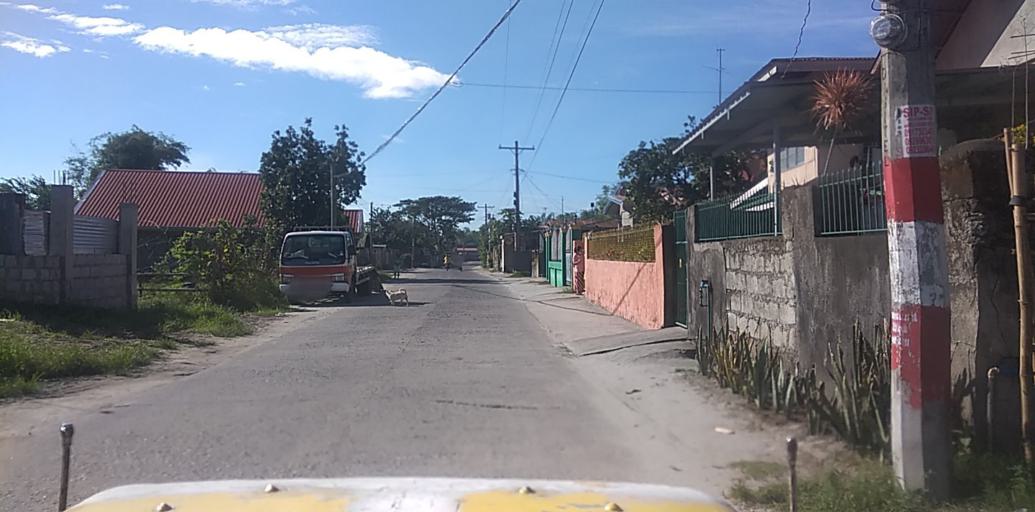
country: PH
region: Central Luzon
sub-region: Province of Pampanga
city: San Patricio
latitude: 15.0950
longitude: 120.7134
